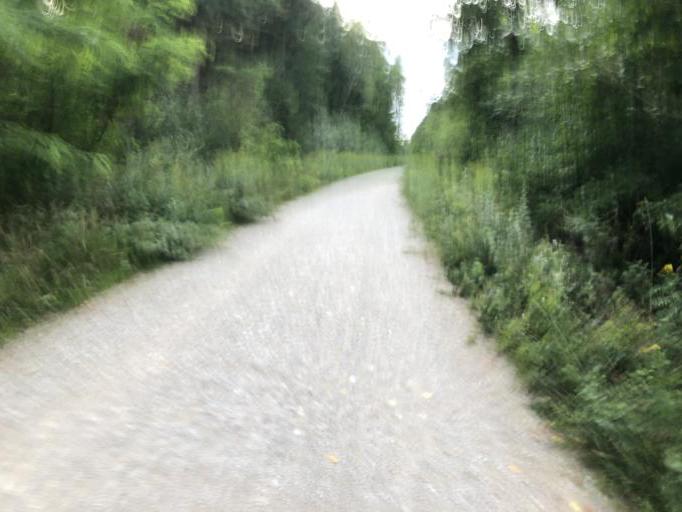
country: DE
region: Bavaria
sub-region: Regierungsbezirk Mittelfranken
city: Buckenhof
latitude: 49.5849
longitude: 11.0477
